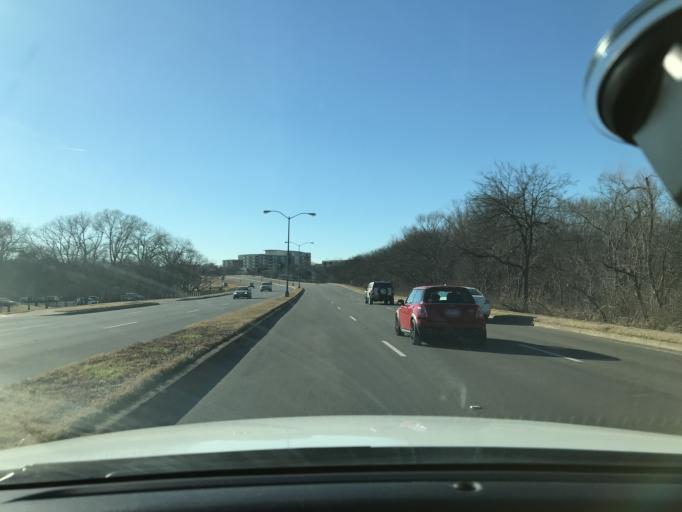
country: US
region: Texas
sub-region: Dallas County
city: Highland Park
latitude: 32.8529
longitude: -96.7243
